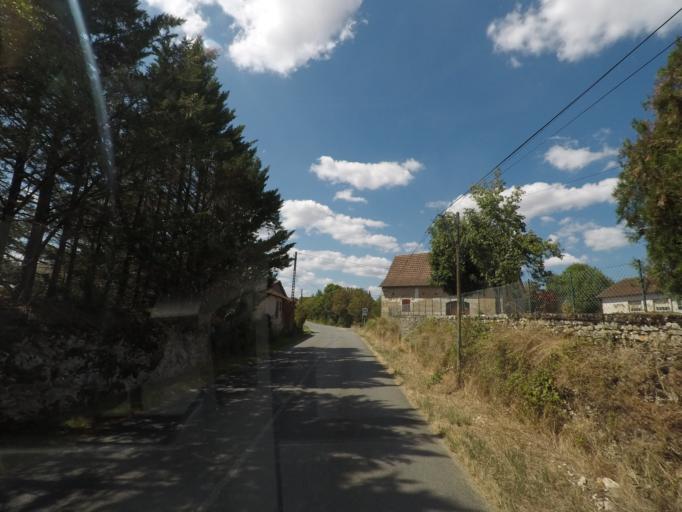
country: FR
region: Midi-Pyrenees
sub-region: Departement du Lot
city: Lacapelle-Marival
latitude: 44.6272
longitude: 1.8247
